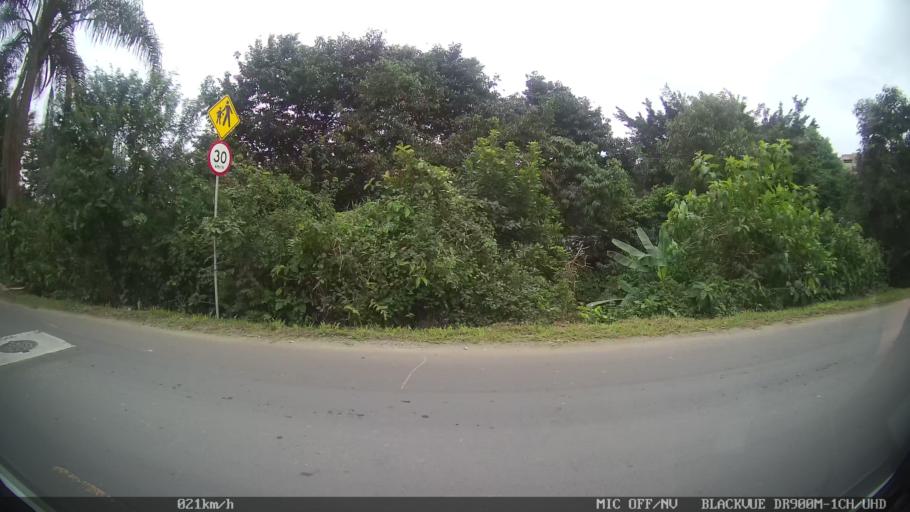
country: BR
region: Santa Catarina
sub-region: Joinville
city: Joinville
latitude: -26.2693
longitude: -48.8686
